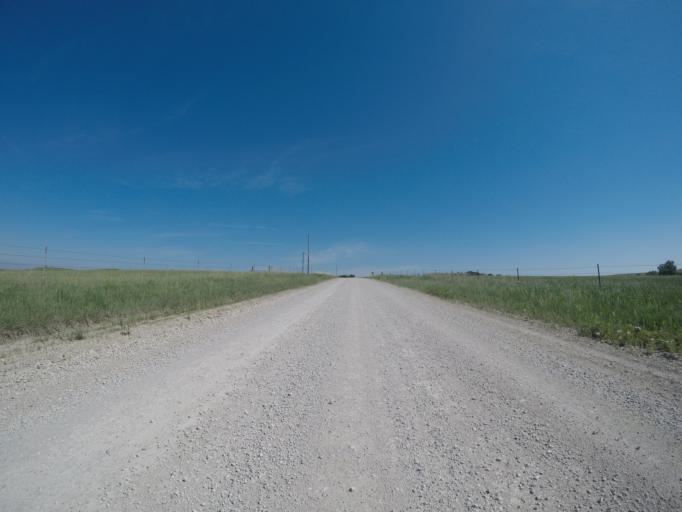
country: US
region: Kansas
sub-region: Wabaunsee County
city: Alma
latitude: 39.0114
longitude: -96.1137
